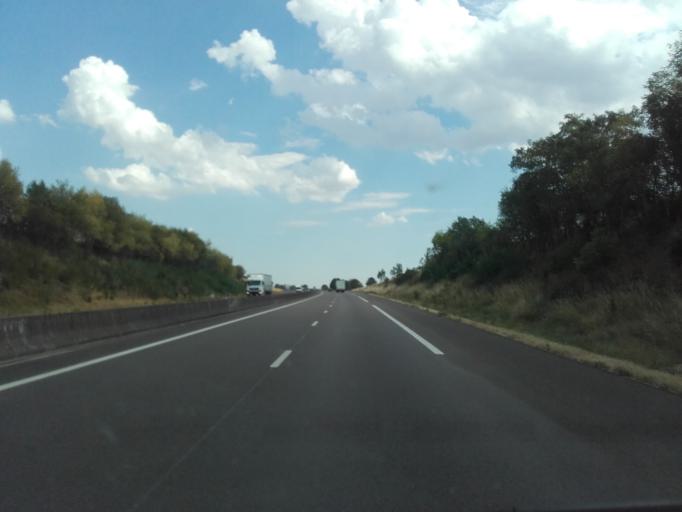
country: FR
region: Bourgogne
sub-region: Departement de la Cote-d'Or
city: Semur-en-Auxois
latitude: 47.4917
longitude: 4.1315
